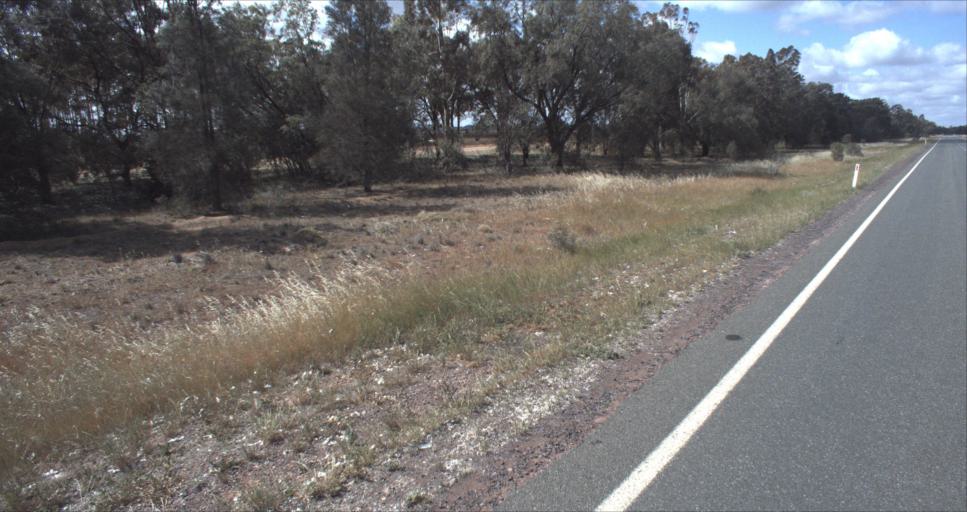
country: AU
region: New South Wales
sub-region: Murrumbidgee Shire
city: Darlington Point
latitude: -34.5861
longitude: 146.1643
